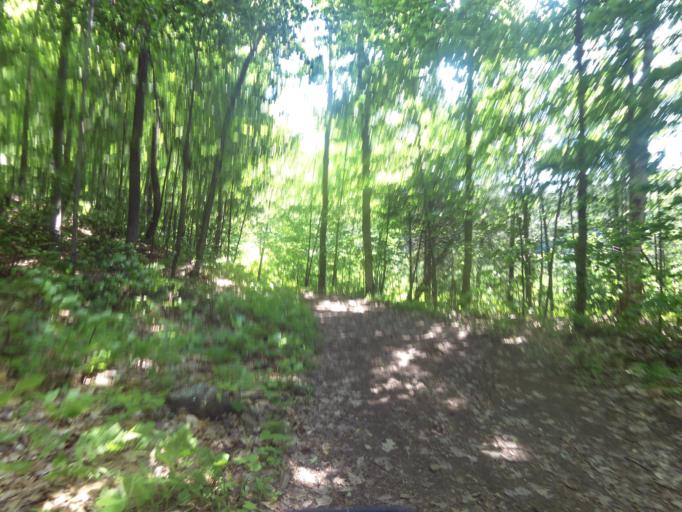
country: CA
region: Quebec
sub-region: Outaouais
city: Wakefield
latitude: 45.5394
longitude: -75.8783
